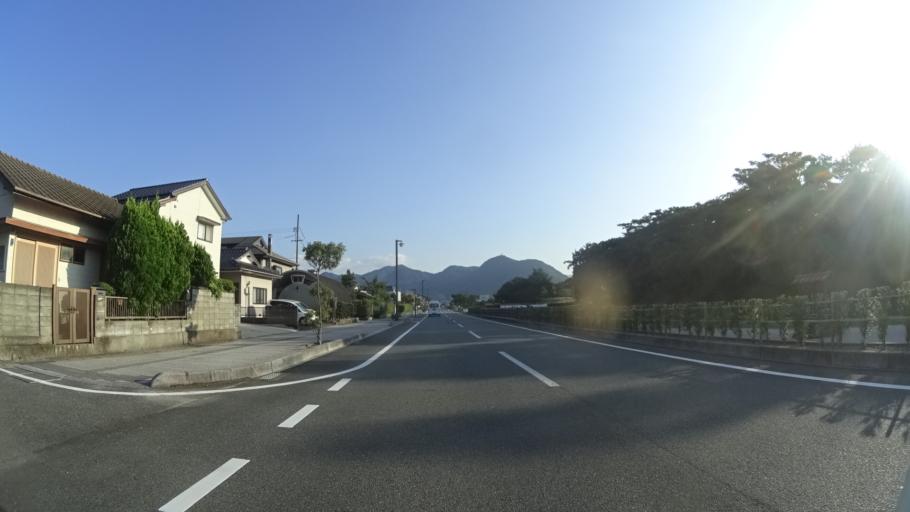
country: JP
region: Yamaguchi
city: Hagi
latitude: 34.4160
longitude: 131.3928
